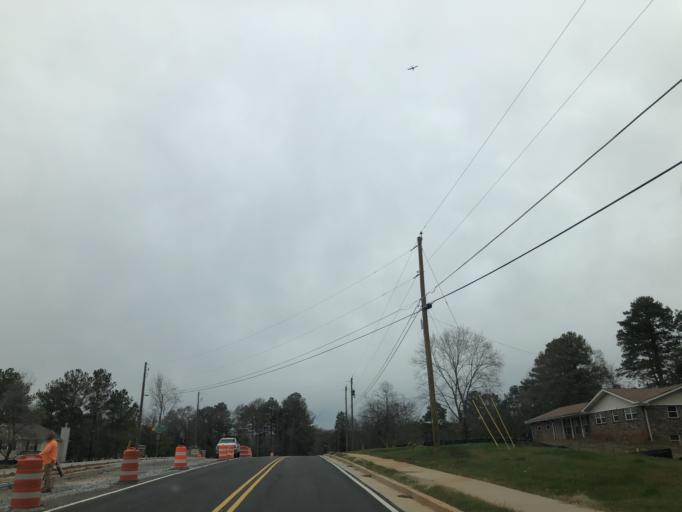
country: US
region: Georgia
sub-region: Clayton County
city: Conley
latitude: 33.6199
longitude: -84.2738
